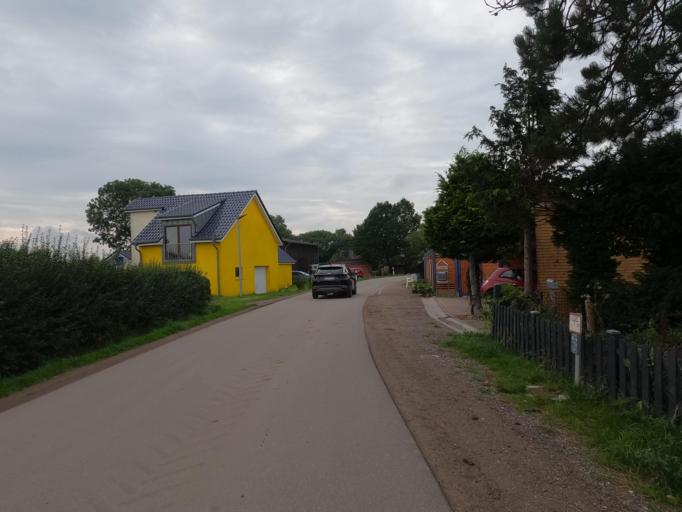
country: DE
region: Schleswig-Holstein
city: Neukirchen
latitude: 54.3244
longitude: 11.0414
